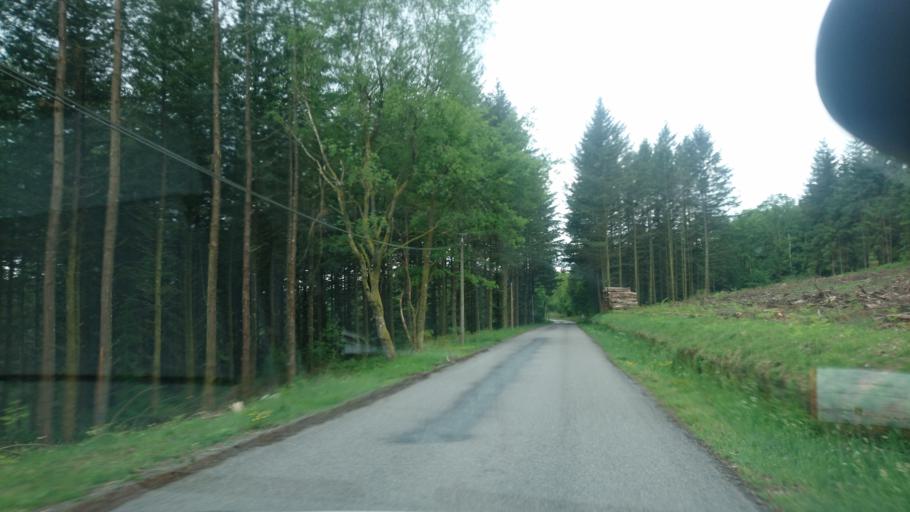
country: FR
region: Limousin
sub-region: Departement de la Haute-Vienne
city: Peyrat-le-Chateau
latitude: 45.8347
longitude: 1.8898
